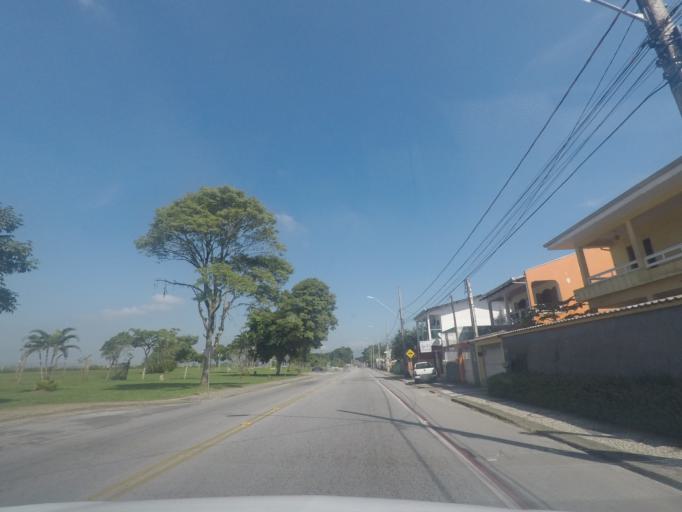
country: BR
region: Parana
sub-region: Paranagua
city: Paranagua
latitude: -25.5346
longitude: -48.5266
